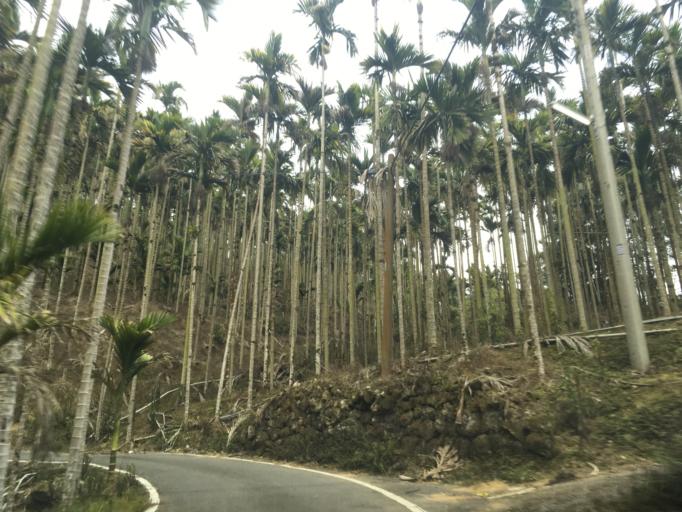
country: TW
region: Taiwan
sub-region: Nantou
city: Puli
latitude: 23.9695
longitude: 120.8283
